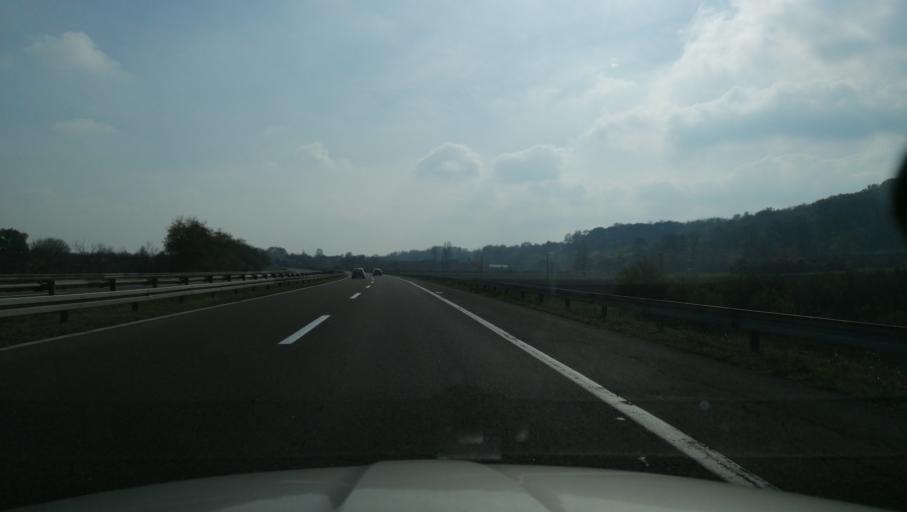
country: RS
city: Lugavcina
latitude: 44.4365
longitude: 21.0504
